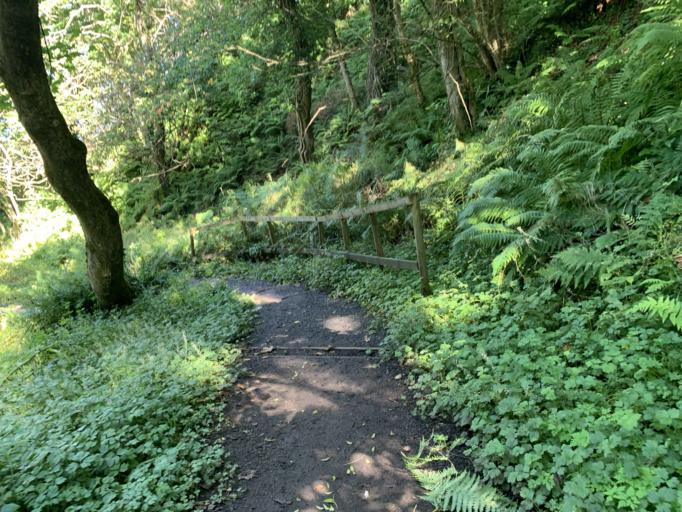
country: GB
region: Scotland
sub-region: South Ayrshire
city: Maybole
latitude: 55.3520
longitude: -4.7952
